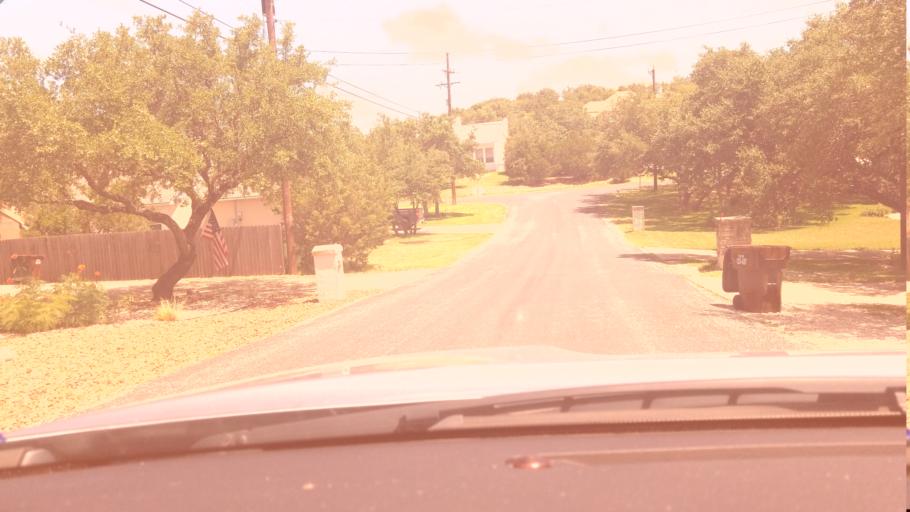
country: US
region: Texas
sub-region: Bexar County
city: Timberwood Park
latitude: 29.6907
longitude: -98.4839
